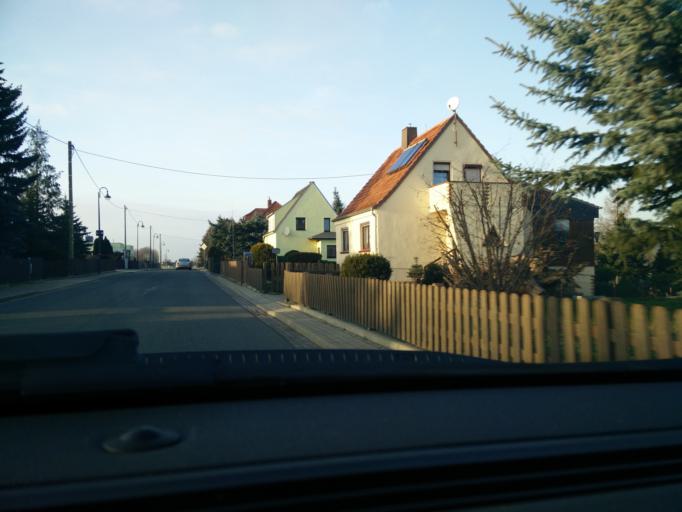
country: DE
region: Saxony
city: Grossbardau
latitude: 51.2377
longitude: 12.6577
